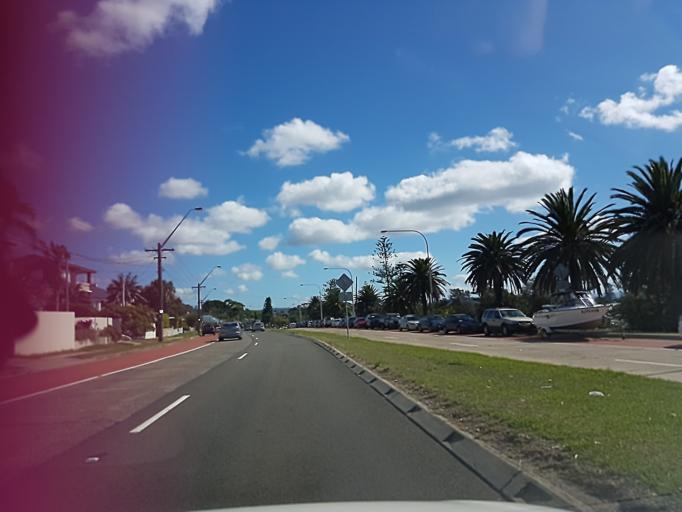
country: AU
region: New South Wales
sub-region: Warringah
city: Dee Why
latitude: -33.7418
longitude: 151.3034
